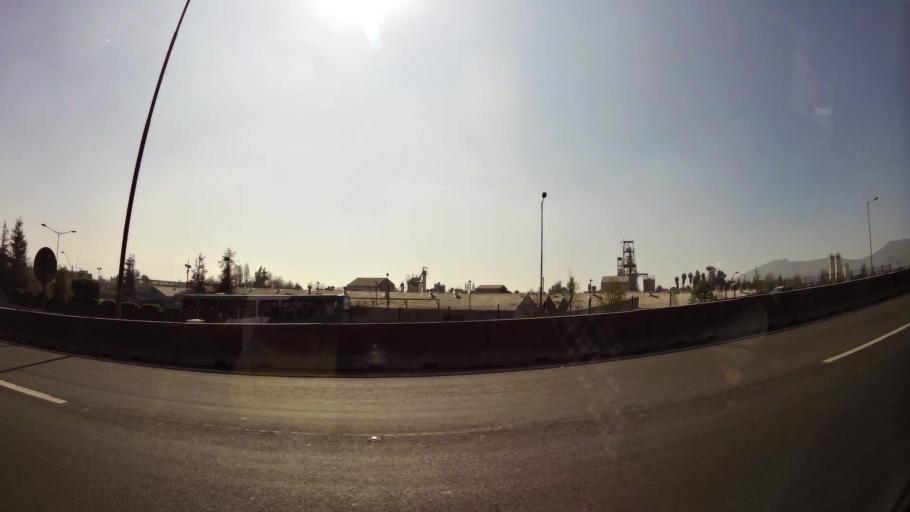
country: CL
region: Santiago Metropolitan
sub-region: Provincia de Santiago
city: Lo Prado
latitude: -33.3685
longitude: -70.7036
